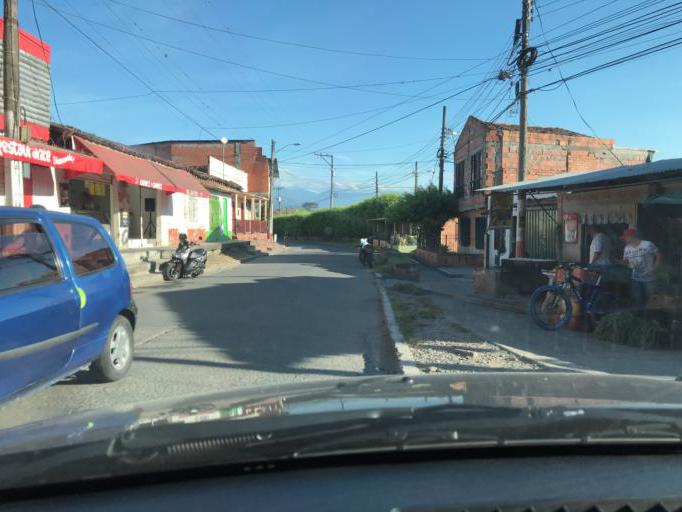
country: CO
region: Valle del Cauca
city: Cartago
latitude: 4.7580
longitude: -75.9311
